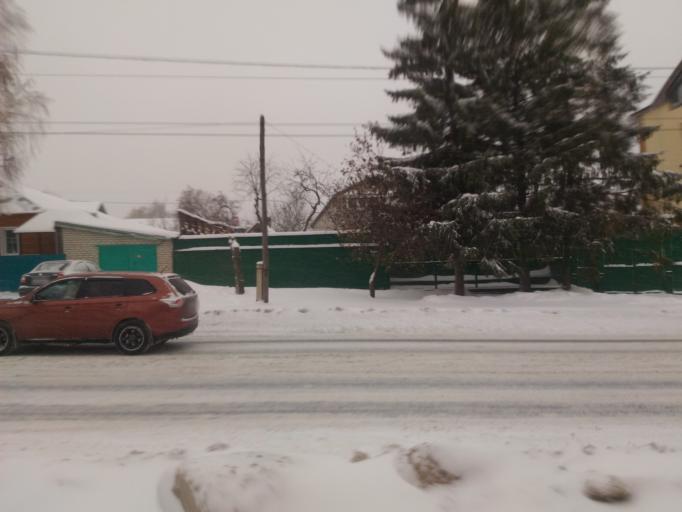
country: RU
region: Ulyanovsk
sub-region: Ulyanovskiy Rayon
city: Ulyanovsk
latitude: 54.3507
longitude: 48.3820
